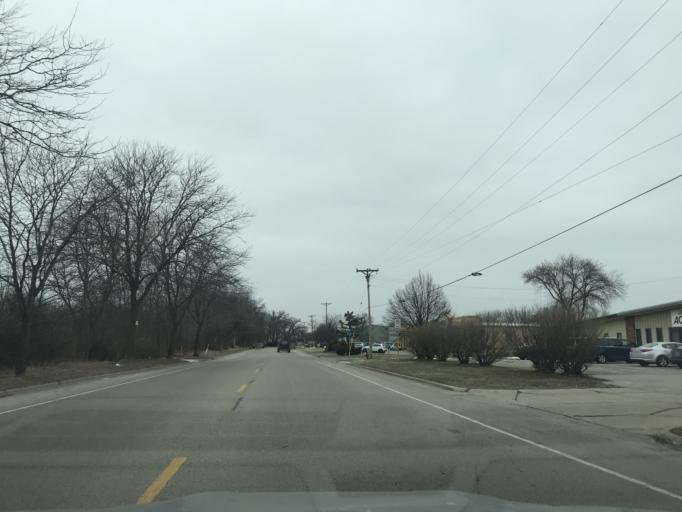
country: US
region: Wisconsin
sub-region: Dane County
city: Monona
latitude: 43.0876
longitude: -89.3109
